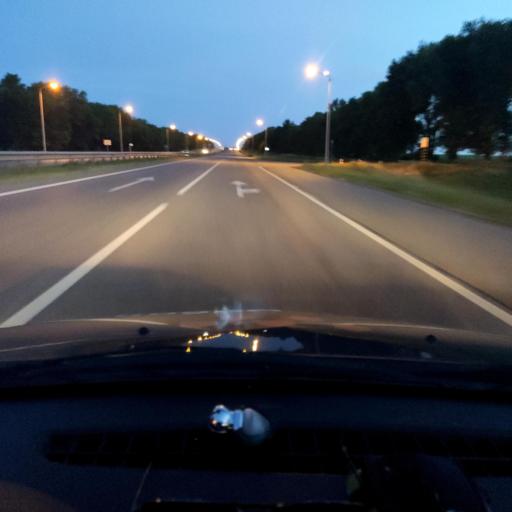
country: RU
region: Belgorod
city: Gubkin
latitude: 51.2501
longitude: 37.5233
